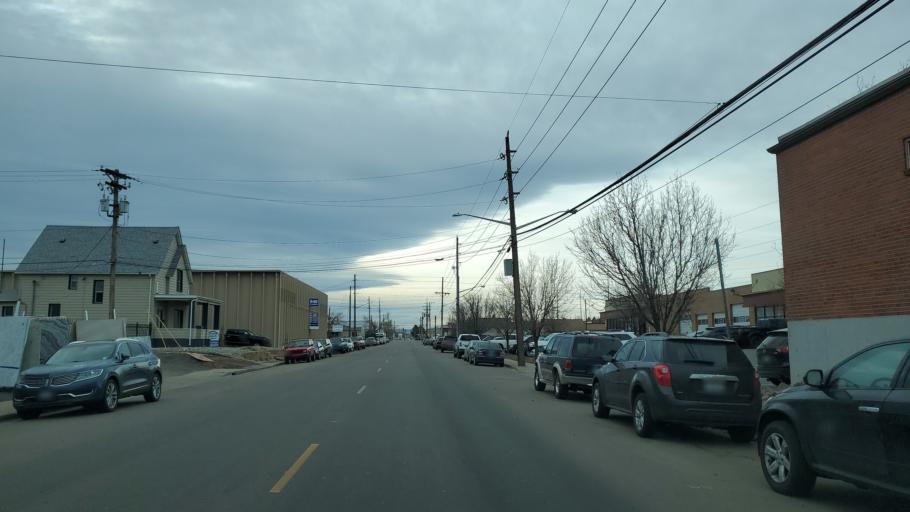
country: US
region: Colorado
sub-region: Denver County
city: Denver
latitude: 39.7007
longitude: -104.9992
